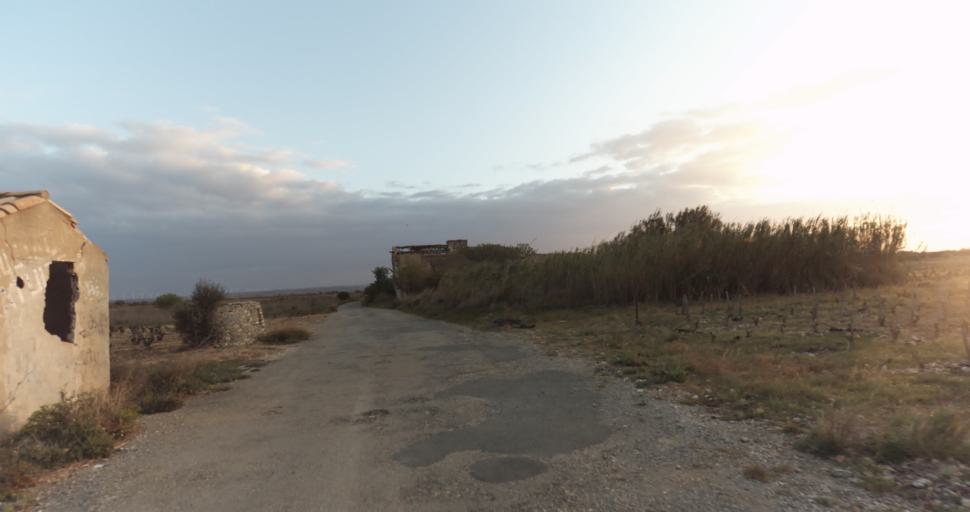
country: FR
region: Languedoc-Roussillon
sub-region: Departement de l'Aude
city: Leucate
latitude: 42.9357
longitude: 3.0044
